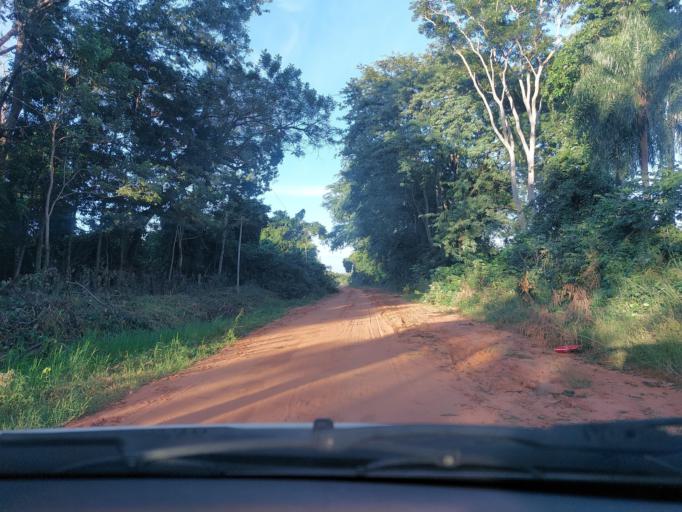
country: PY
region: San Pedro
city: Itacurubi del Rosario
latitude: -24.5398
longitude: -56.5817
